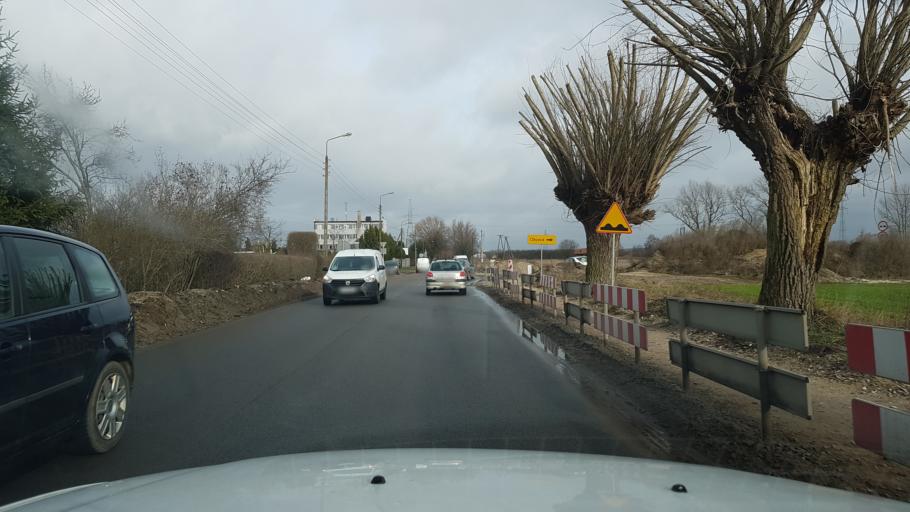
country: PL
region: West Pomeranian Voivodeship
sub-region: Powiat szczecinecki
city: Szczecinek
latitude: 53.7152
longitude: 16.7165
